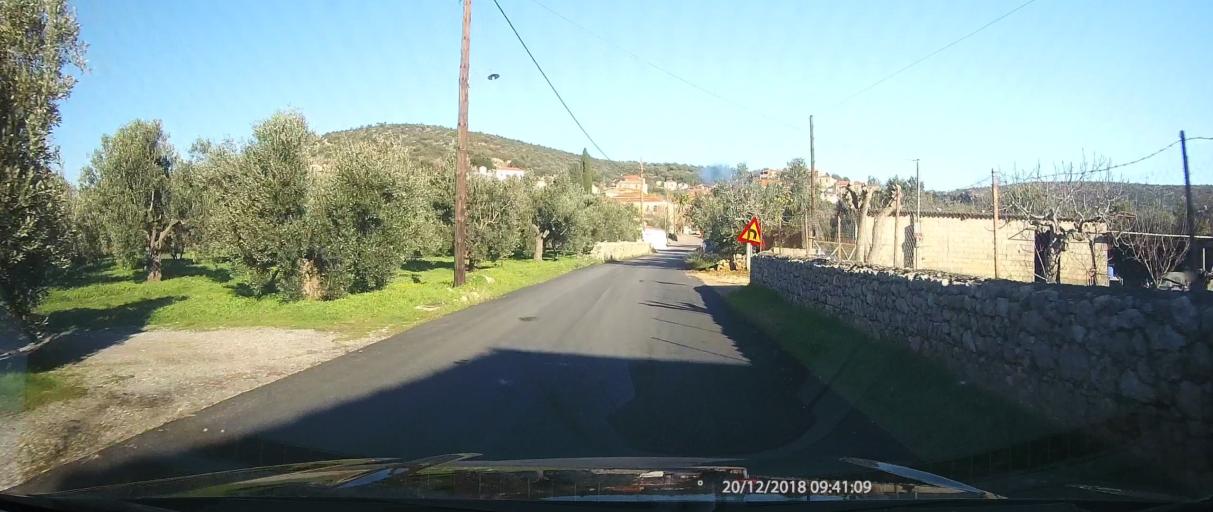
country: GR
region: Peloponnese
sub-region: Nomos Lakonias
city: Yerakion
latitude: 36.9515
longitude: 22.7658
